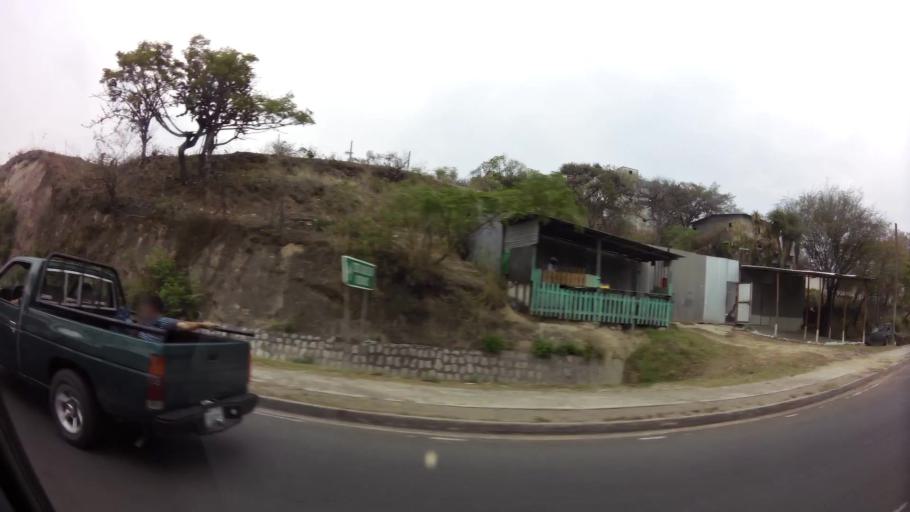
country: HN
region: Francisco Morazan
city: El Tablon
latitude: 14.0454
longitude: -87.1879
